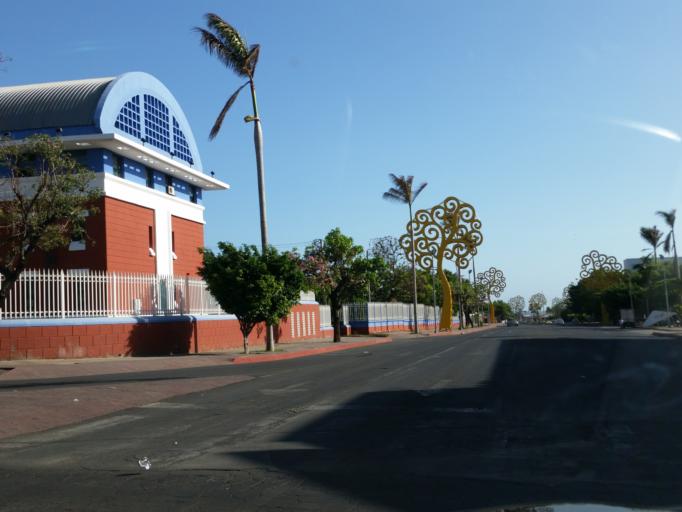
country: NI
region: Managua
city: Managua
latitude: 12.1548
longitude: -86.2738
